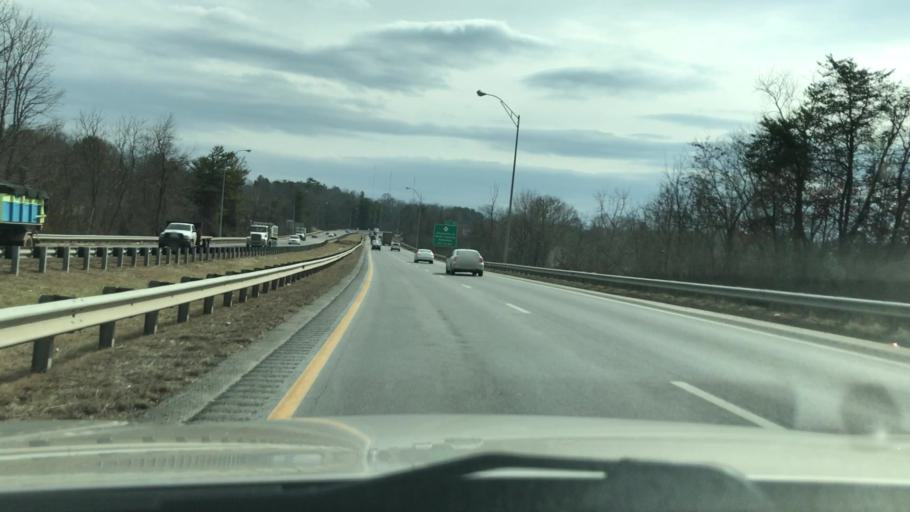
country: US
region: North Carolina
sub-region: Buncombe County
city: Woodfin
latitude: 35.6257
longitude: -82.5782
